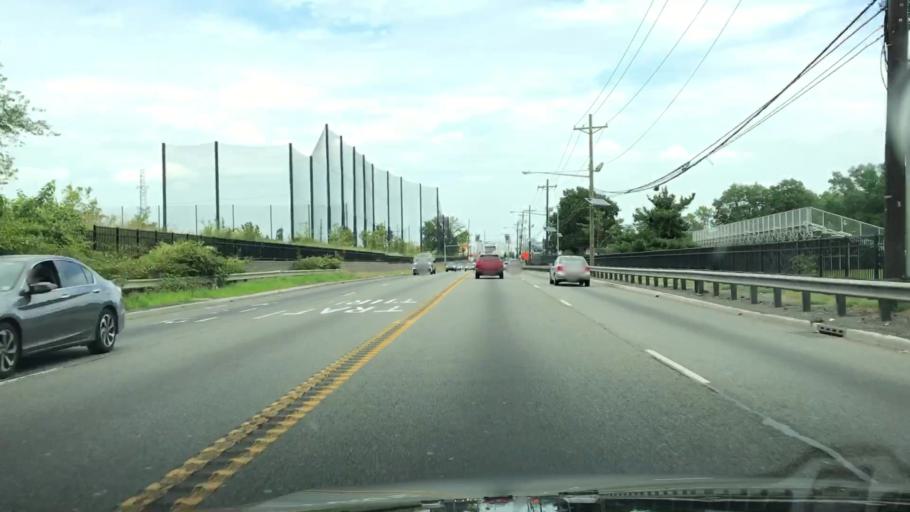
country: US
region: New Jersey
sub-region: Hudson County
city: Jersey City
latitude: 40.7275
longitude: -74.0873
